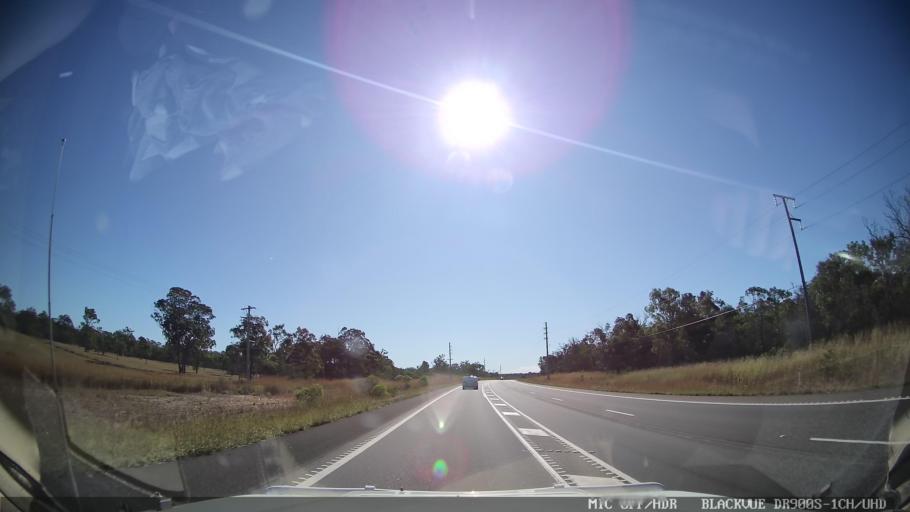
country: AU
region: Queensland
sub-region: Bundaberg
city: Childers
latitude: -25.2732
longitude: 152.3801
